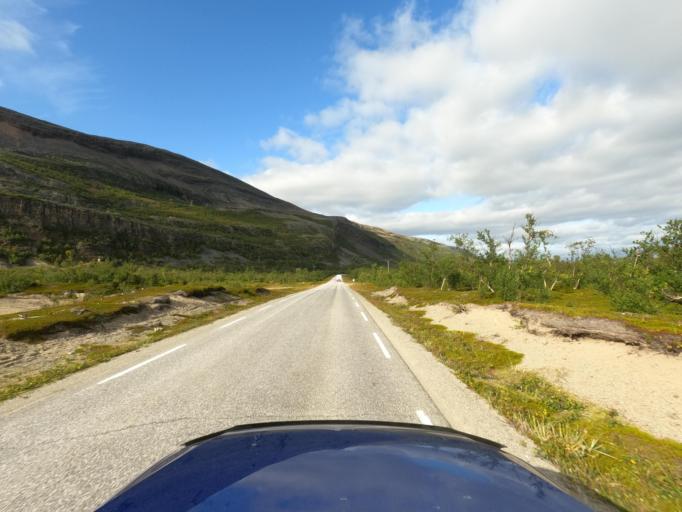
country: NO
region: Finnmark Fylke
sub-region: Porsanger
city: Lakselv
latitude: 70.0777
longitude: 24.9208
